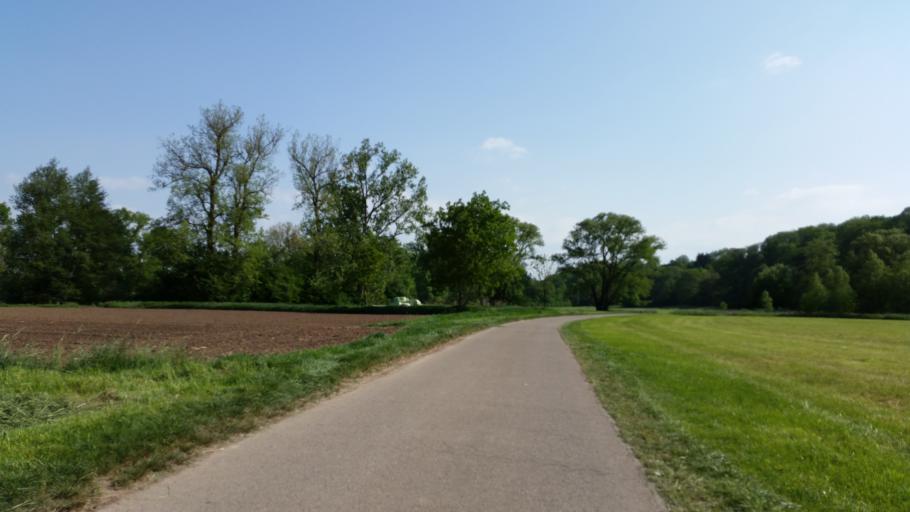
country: DE
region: Baden-Wuerttemberg
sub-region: Regierungsbezirk Stuttgart
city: Pleidelsheim
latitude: 48.9519
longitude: 9.1833
